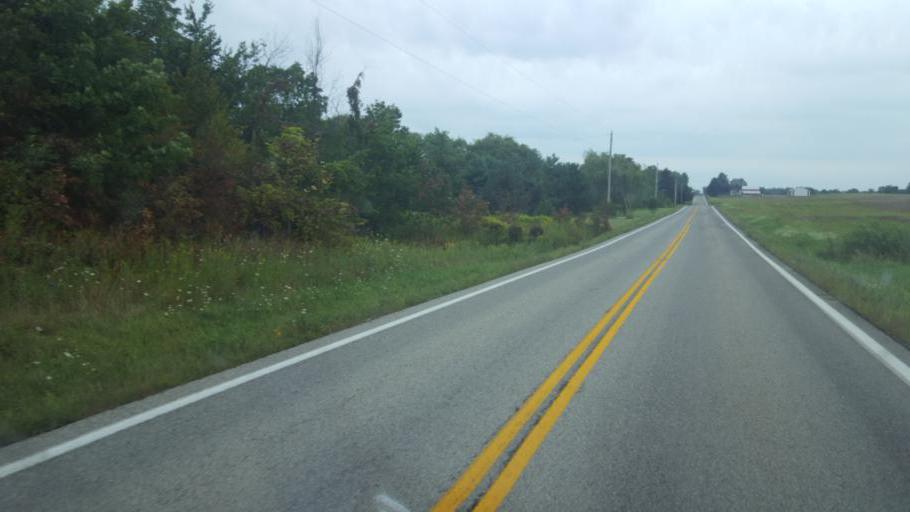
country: US
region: Ohio
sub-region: Morrow County
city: Mount Gilead
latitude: 40.6026
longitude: -82.7662
